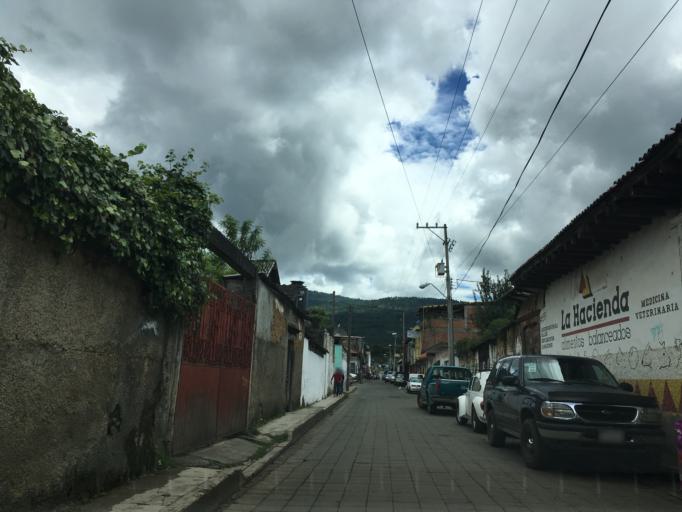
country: MX
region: Michoacan
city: Nahuatzen
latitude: 19.6536
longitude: -101.9174
